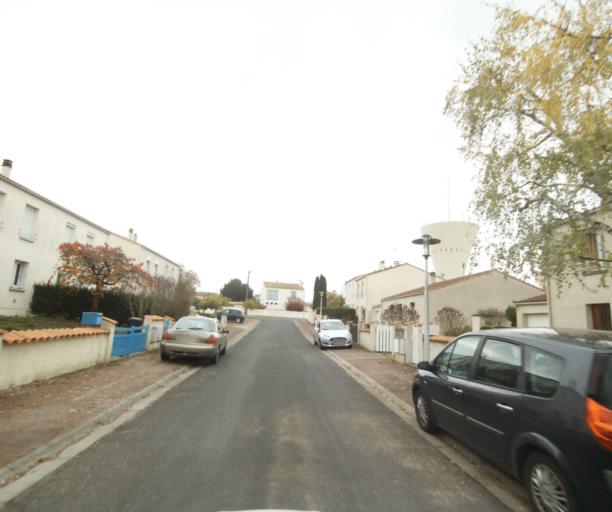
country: FR
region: Poitou-Charentes
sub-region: Departement de la Charente-Maritime
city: Saintes
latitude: 45.7327
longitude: -0.6524
